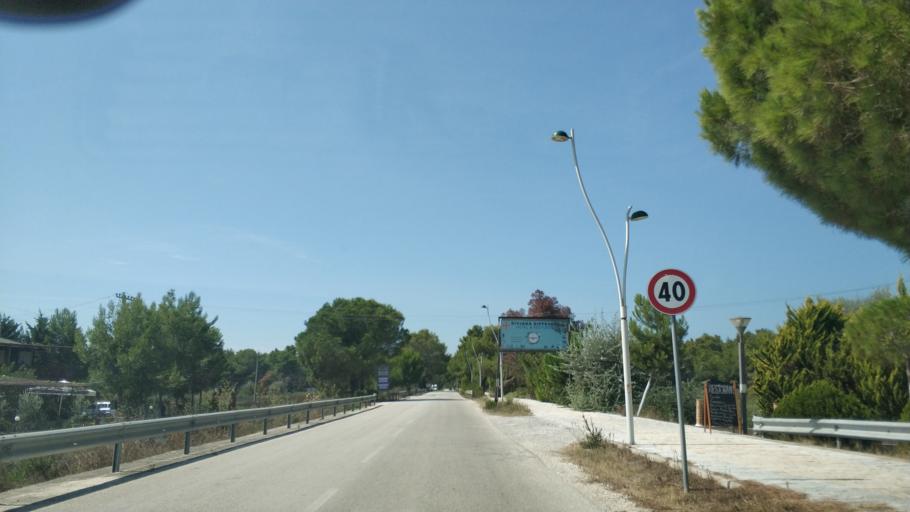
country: AL
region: Fier
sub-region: Rrethi i Lushnjes
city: Divjake
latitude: 40.9905
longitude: 19.4997
